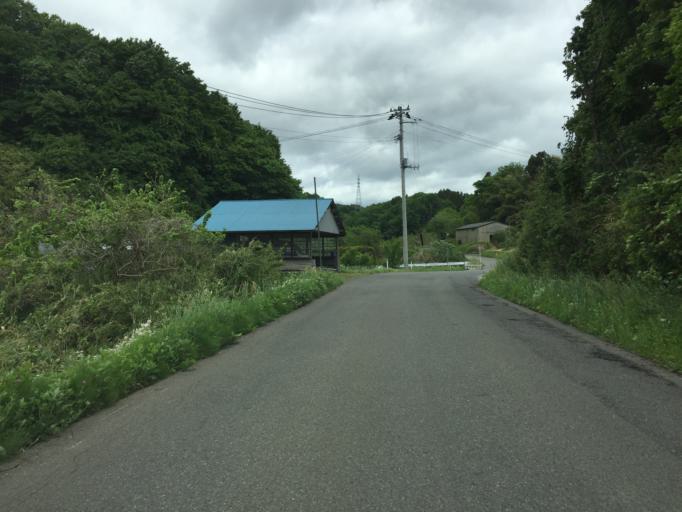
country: JP
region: Fukushima
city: Miharu
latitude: 37.4603
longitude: 140.4701
